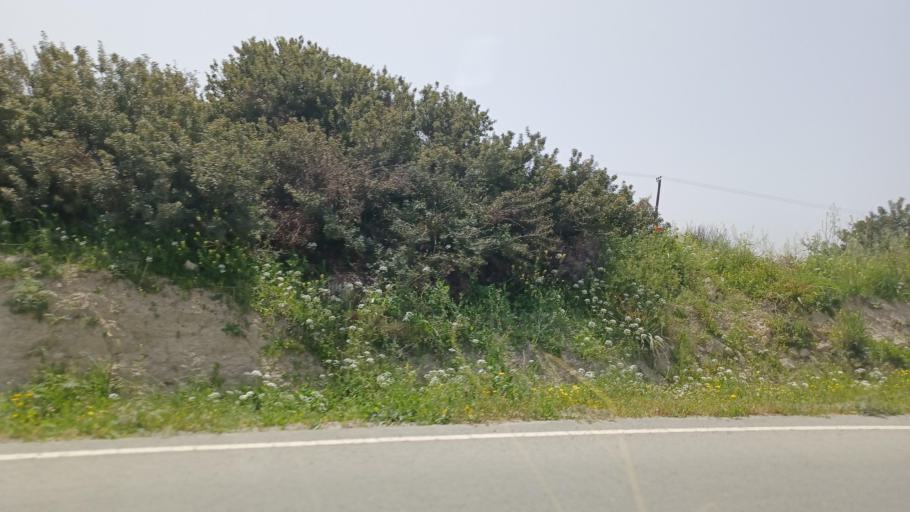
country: CY
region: Limassol
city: Pissouri
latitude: 34.7021
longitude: 32.7508
